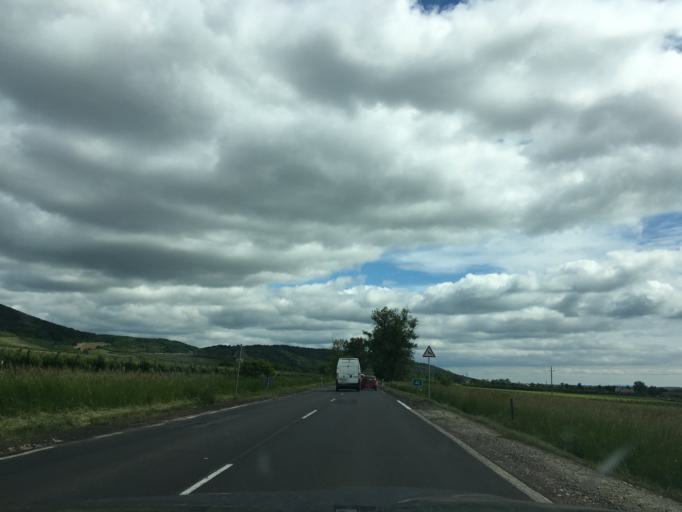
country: HU
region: Borsod-Abauj-Zemplen
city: Tarcal
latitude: 48.1901
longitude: 21.3650
